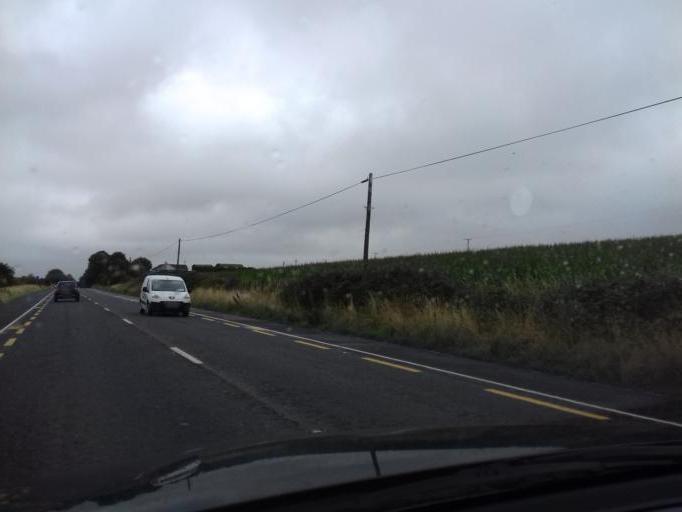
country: IE
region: Leinster
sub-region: County Carlow
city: Bagenalstown
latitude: 52.7510
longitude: -6.9635
